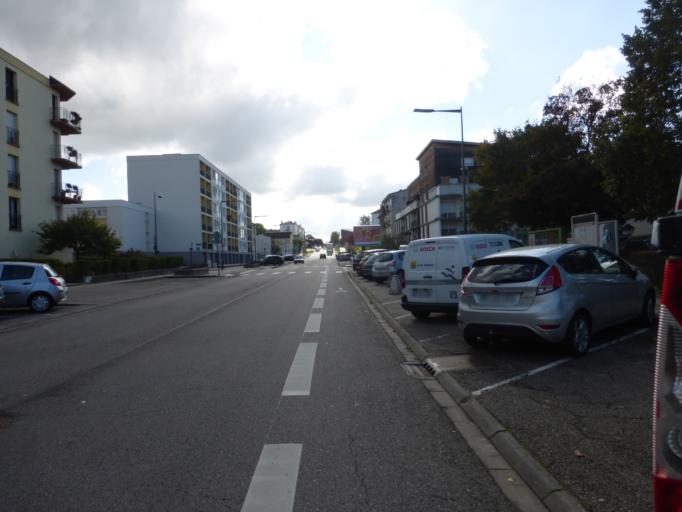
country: FR
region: Lorraine
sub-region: Departement de Meurthe-et-Moselle
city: Villers-les-Nancy
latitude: 48.6729
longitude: 6.1604
